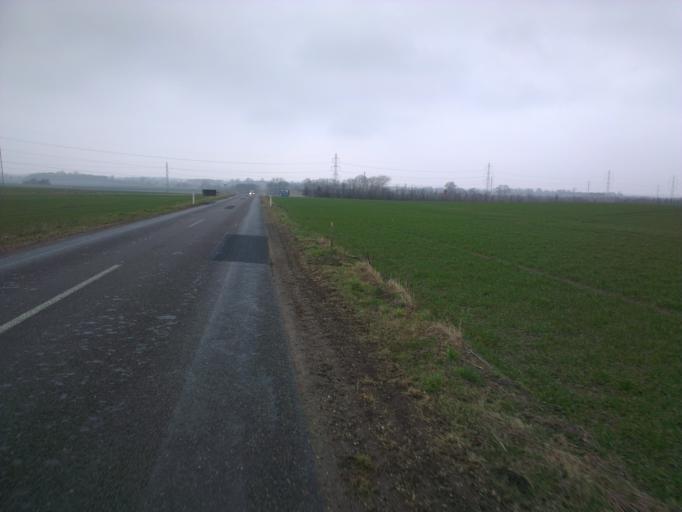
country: DK
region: Capital Region
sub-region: Frederikssund Kommune
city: Skibby
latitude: 55.7987
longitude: 11.9610
